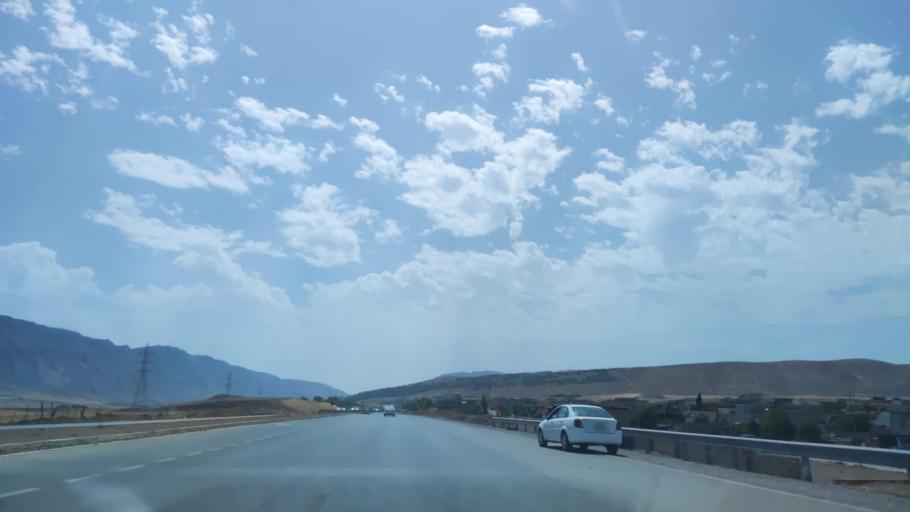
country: IQ
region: Arbil
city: Shaqlawah
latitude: 36.5059
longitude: 44.3506
